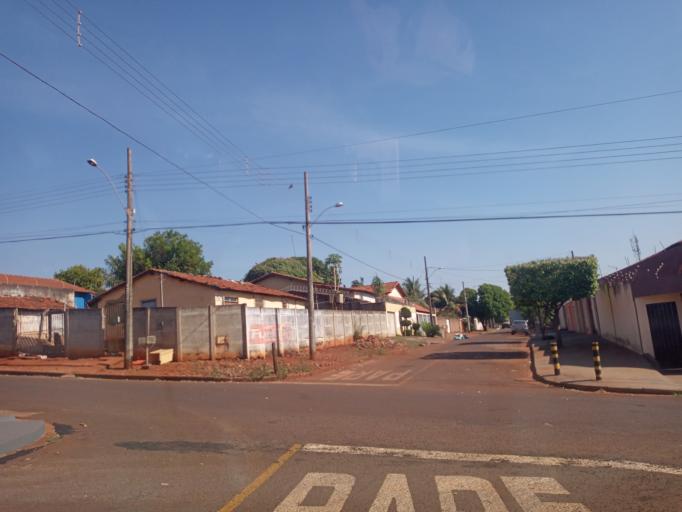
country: BR
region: Minas Gerais
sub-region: Ituiutaba
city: Ituiutaba
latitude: -18.9519
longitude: -49.4590
